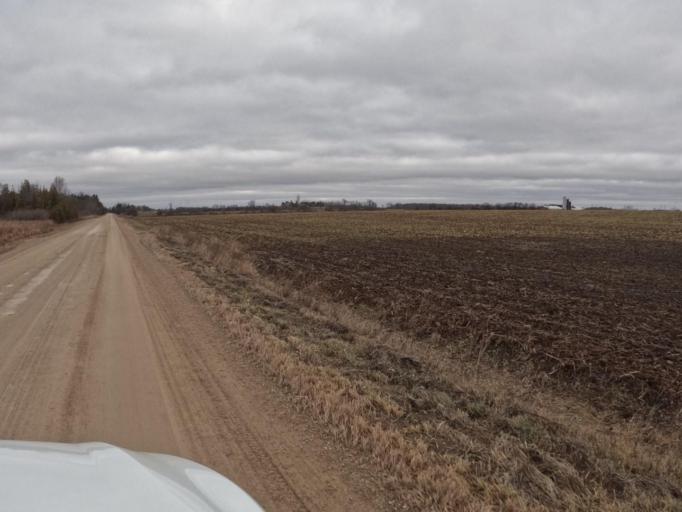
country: CA
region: Ontario
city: Shelburne
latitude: 43.9491
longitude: -80.3964
